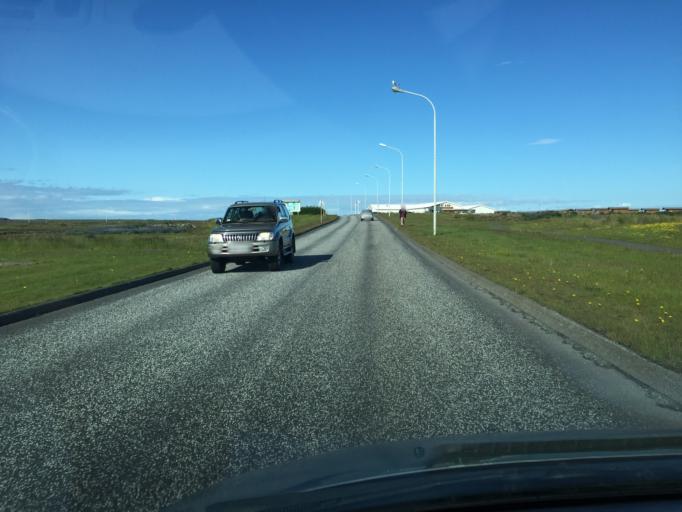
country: IS
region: Southern Peninsula
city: Reykjanesbaer
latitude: 63.9997
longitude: -22.5798
